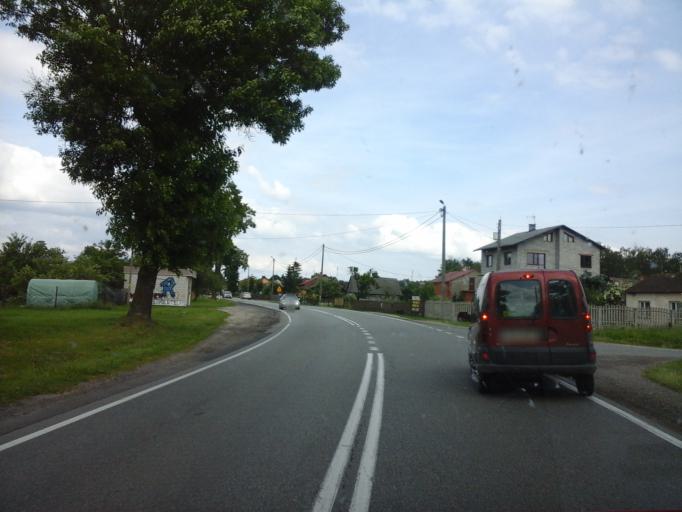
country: PL
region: Lodz Voivodeship
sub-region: Powiat opoczynski
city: Paradyz
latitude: 51.3145
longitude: 20.0687
